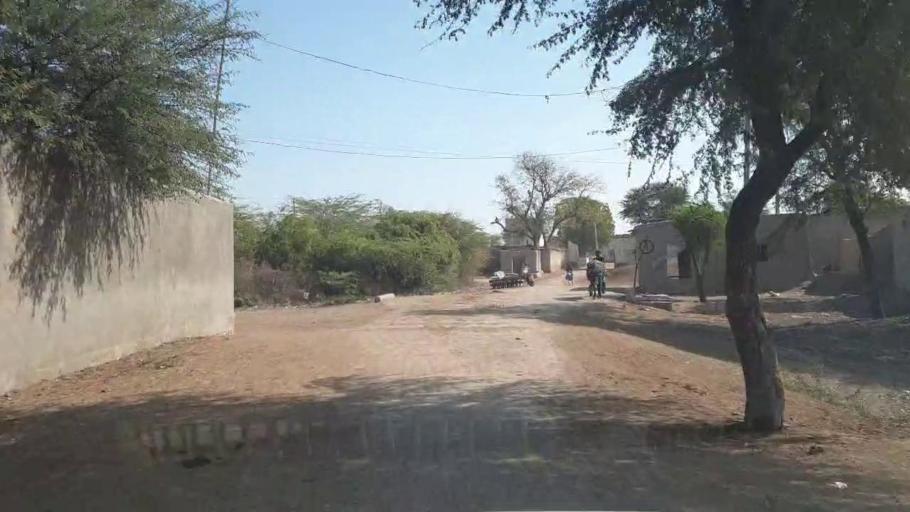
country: PK
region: Sindh
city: Umarkot
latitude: 25.3076
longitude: 69.6593
